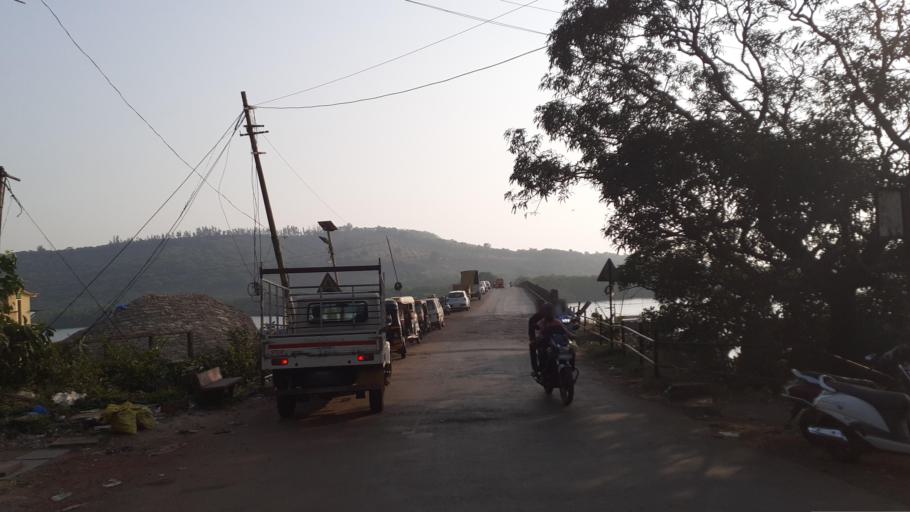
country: IN
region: Maharashtra
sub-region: Ratnagiri
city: Ratnagiri
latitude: 17.0420
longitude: 73.2978
